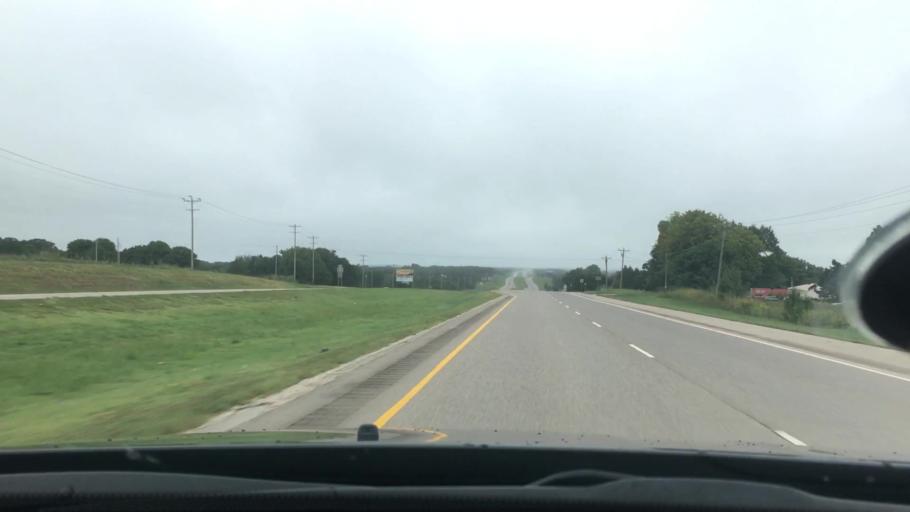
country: US
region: Oklahoma
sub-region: Seminole County
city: Seminole
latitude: 35.3170
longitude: -96.6713
